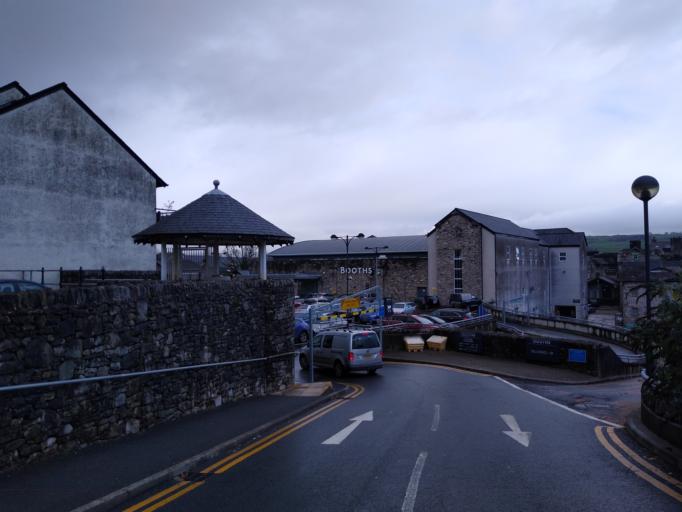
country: GB
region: England
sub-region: Cumbria
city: Kendal
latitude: 54.3277
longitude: -2.7500
